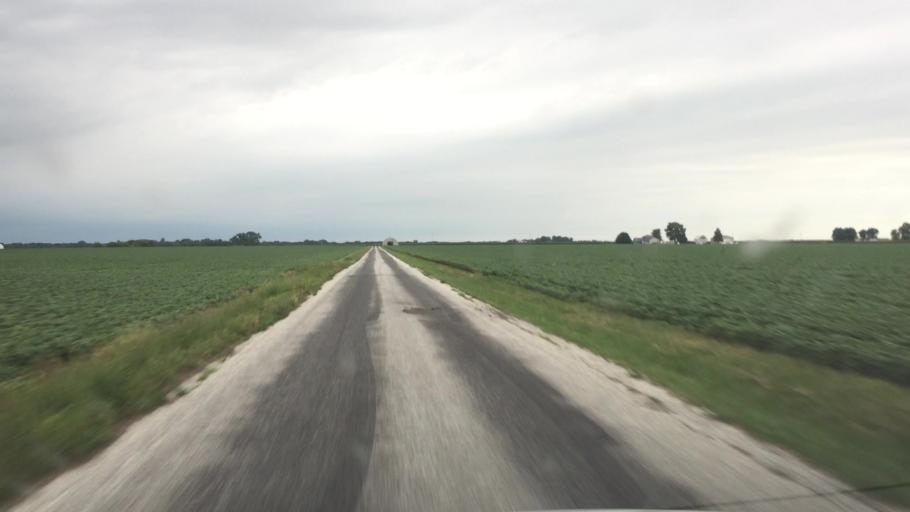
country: US
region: Illinois
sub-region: Adams County
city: Camp Point
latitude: 40.2232
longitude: -90.9691
